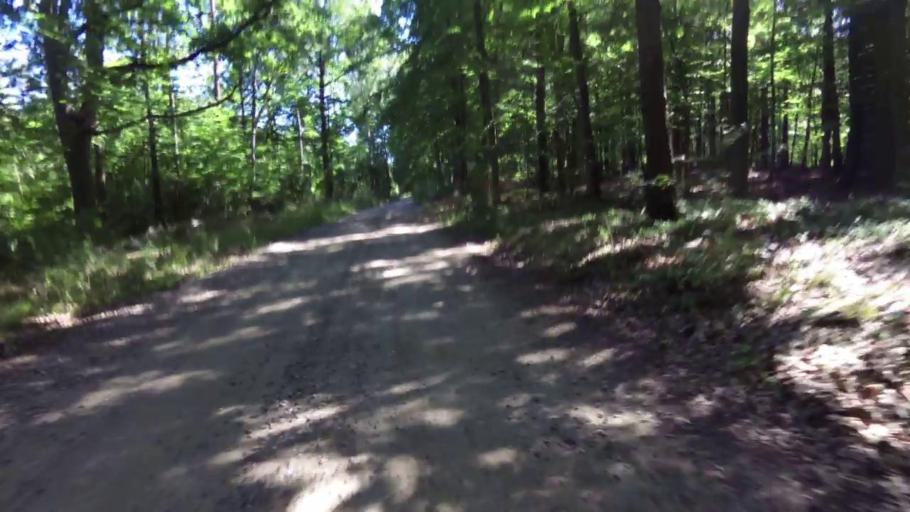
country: PL
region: West Pomeranian Voivodeship
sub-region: Powiat drawski
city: Wierzchowo
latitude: 53.5269
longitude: 16.1027
